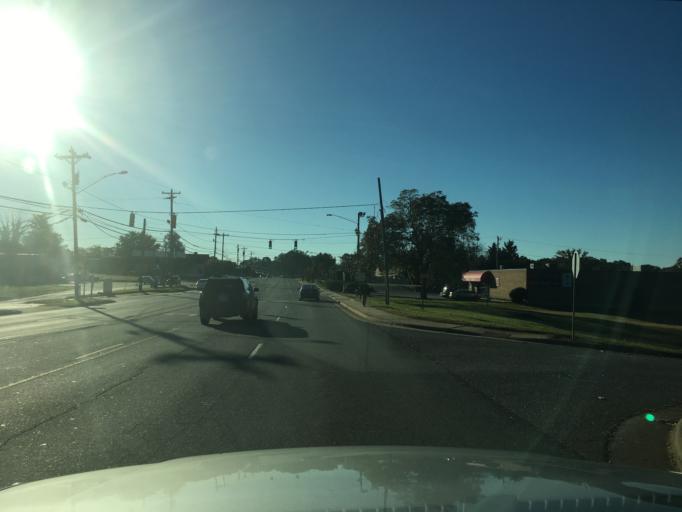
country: US
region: North Carolina
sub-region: Catawba County
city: Hickory
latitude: 35.7279
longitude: -81.3242
